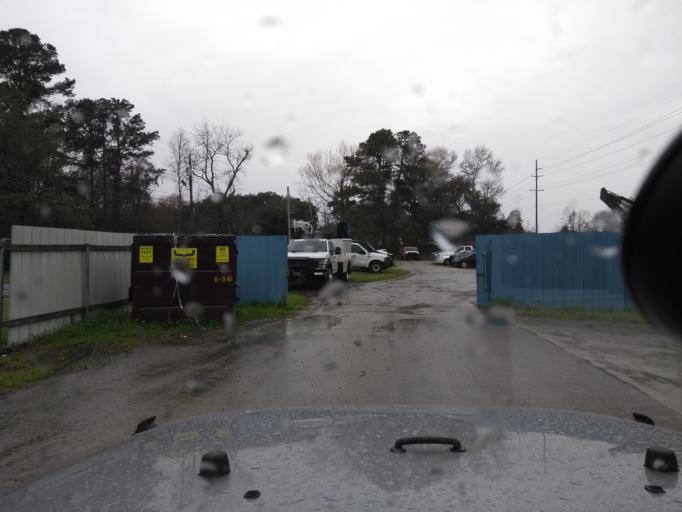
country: US
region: Georgia
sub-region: Chatham County
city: Garden City
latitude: 32.0916
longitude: -81.1598
